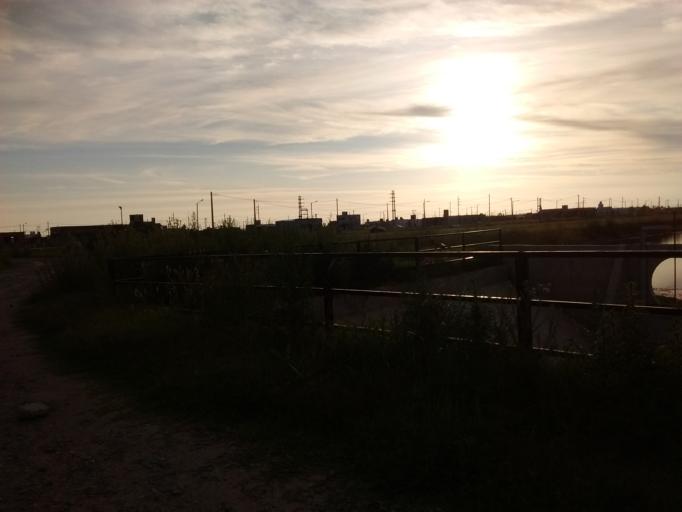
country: AR
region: Santa Fe
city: Roldan
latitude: -32.9418
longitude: -60.8752
